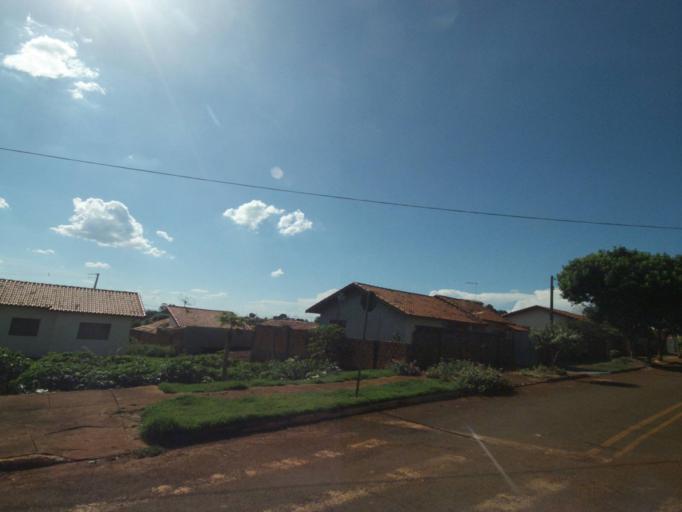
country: BR
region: Parana
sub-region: Sertanopolis
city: Sertanopolis
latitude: -23.0468
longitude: -50.8183
